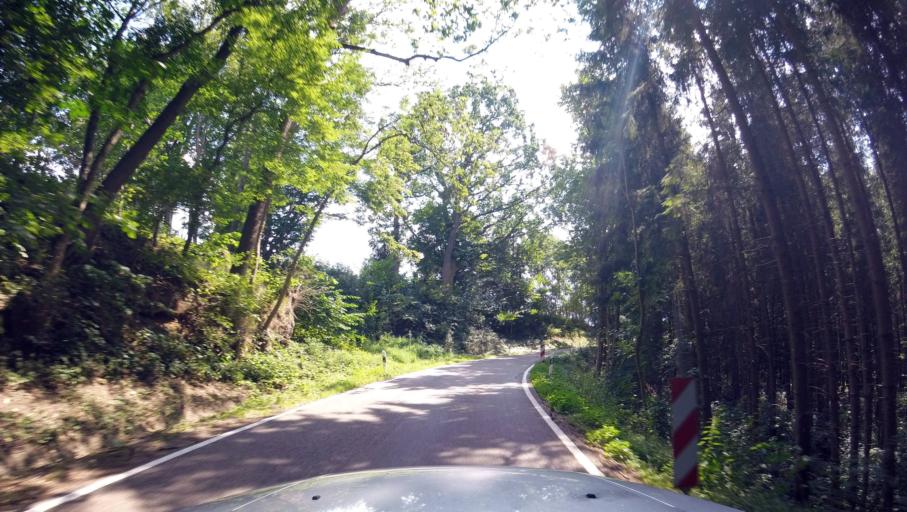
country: DE
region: Baden-Wuerttemberg
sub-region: Regierungsbezirk Stuttgart
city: Alfdorf
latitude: 48.8898
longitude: 9.7114
